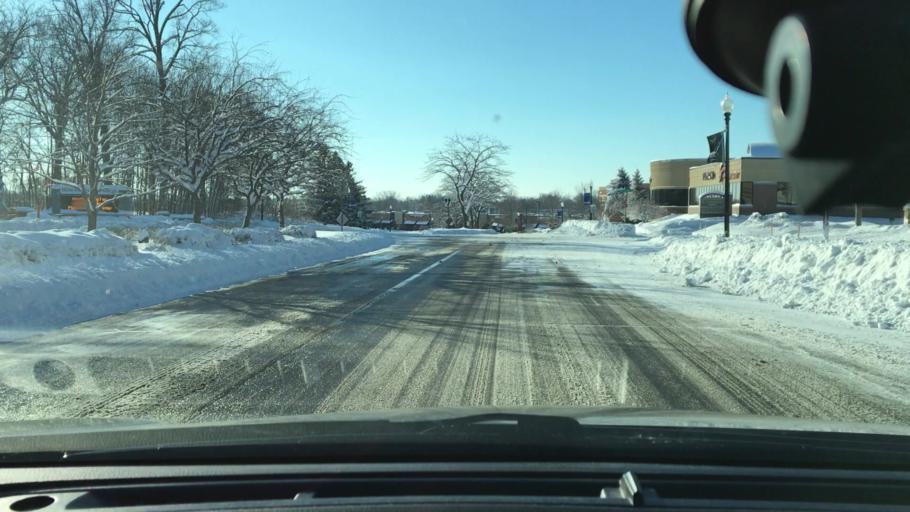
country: US
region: Minnesota
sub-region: Hennepin County
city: Plymouth
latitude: 45.0208
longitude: -93.4772
